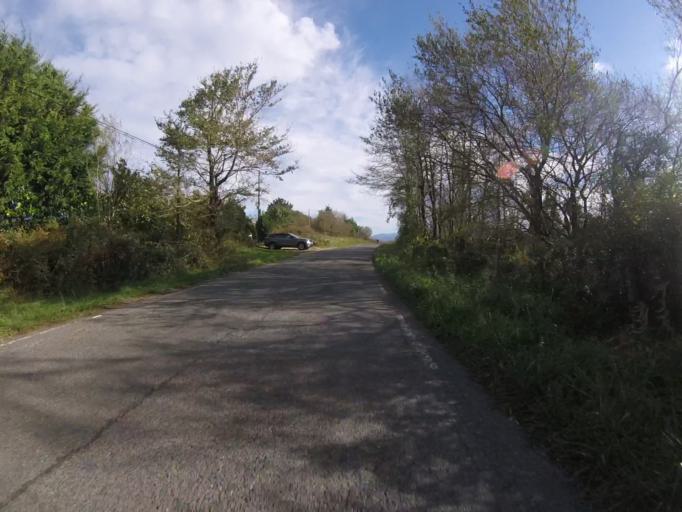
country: ES
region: Basque Country
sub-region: Provincia de Guipuzcoa
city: Usurbil
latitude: 43.2997
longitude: -2.0614
